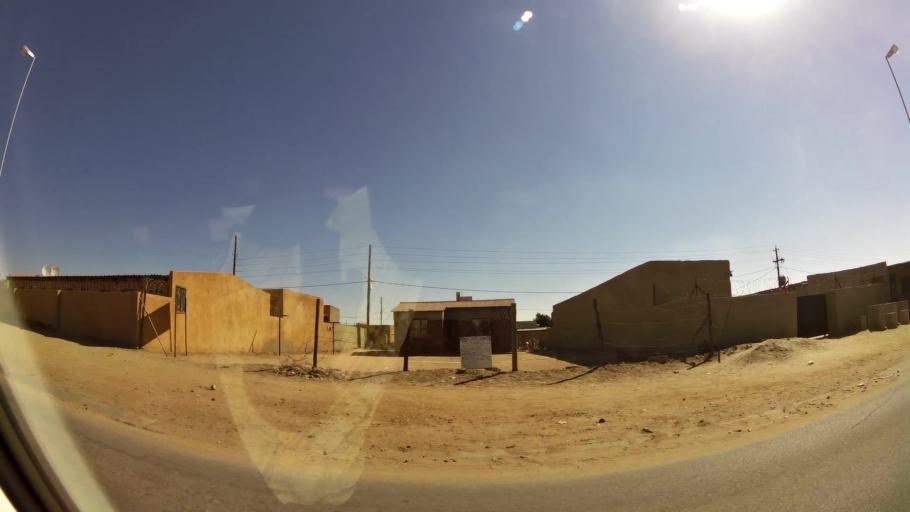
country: ZA
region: Limpopo
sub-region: Capricorn District Municipality
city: Polokwane
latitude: -23.8586
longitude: 29.4122
